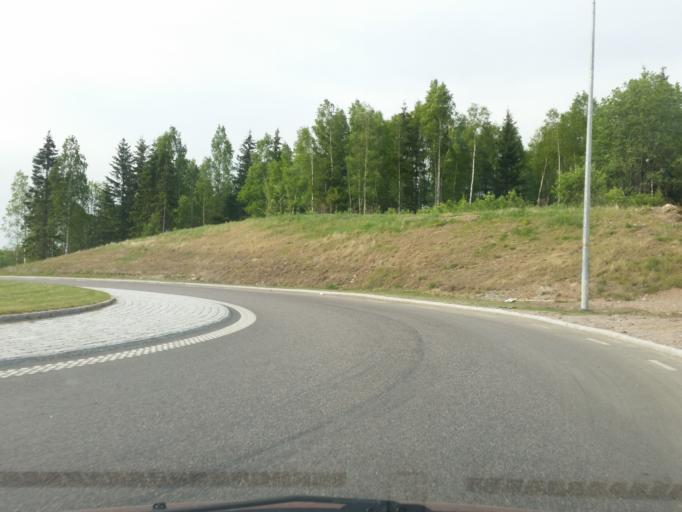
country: SE
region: Vaestra Goetaland
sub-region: Ulricehamns Kommun
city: Ulricehamn
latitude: 57.8068
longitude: 13.4536
